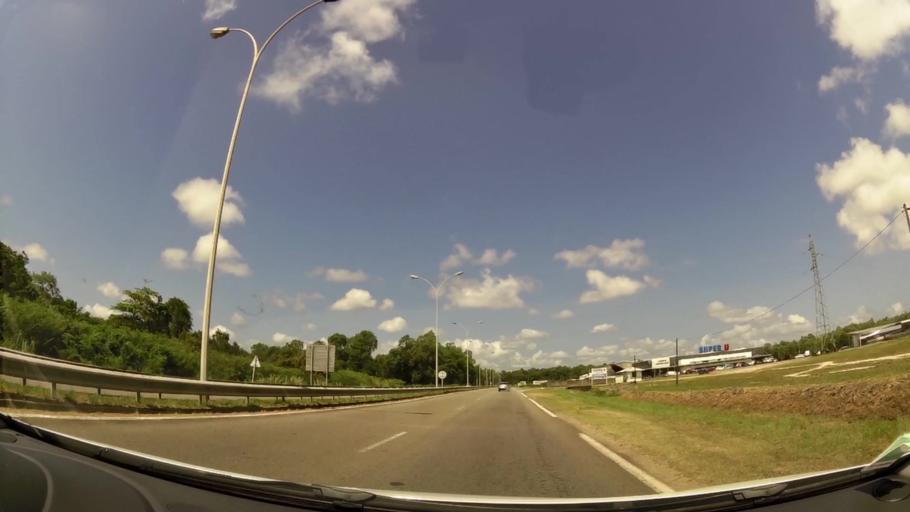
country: GF
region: Guyane
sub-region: Guyane
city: Cayenne
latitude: 4.9240
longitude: -52.3250
